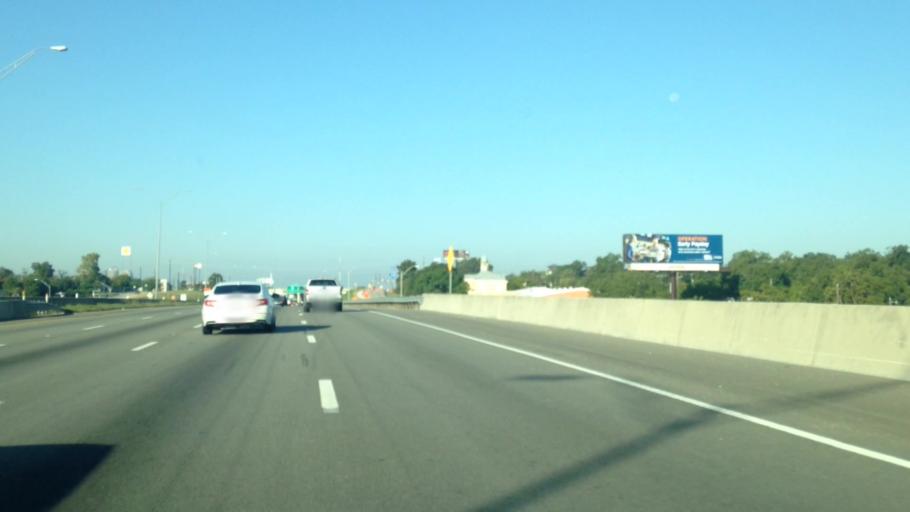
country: US
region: Texas
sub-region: Bexar County
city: Terrell Hills
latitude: 29.4392
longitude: -98.4550
